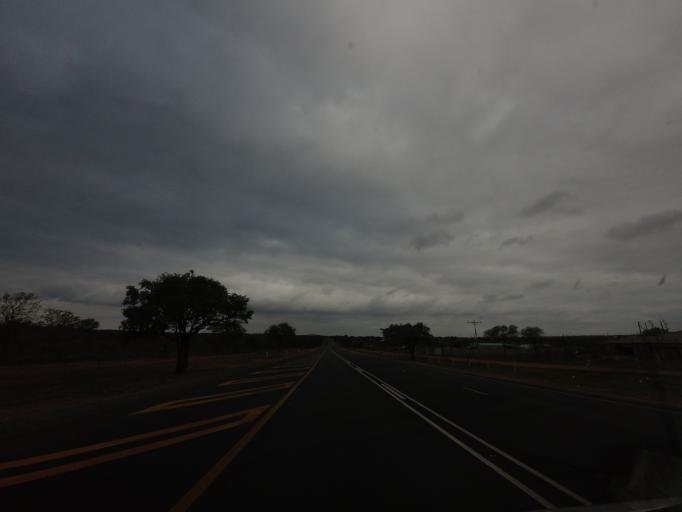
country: ZA
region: Mpumalanga
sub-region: Ehlanzeni District
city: Komatipoort
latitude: -25.4423
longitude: 31.7012
